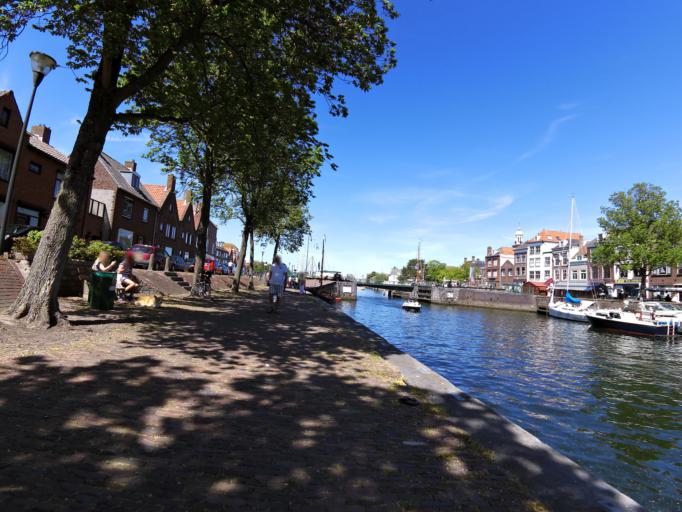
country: NL
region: South Holland
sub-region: Gemeente Hellevoetsluis
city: Hellevoetsluis
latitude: 51.8222
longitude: 4.1282
